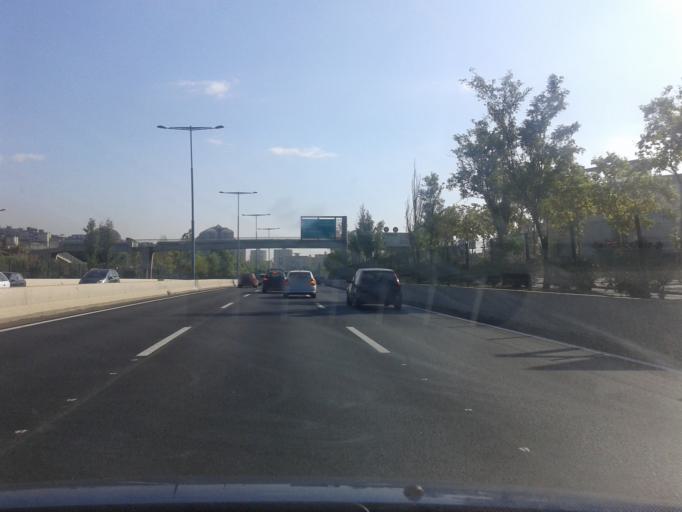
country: ES
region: Catalonia
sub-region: Provincia de Barcelona
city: Nou Barris
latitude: 41.4391
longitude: 2.1565
